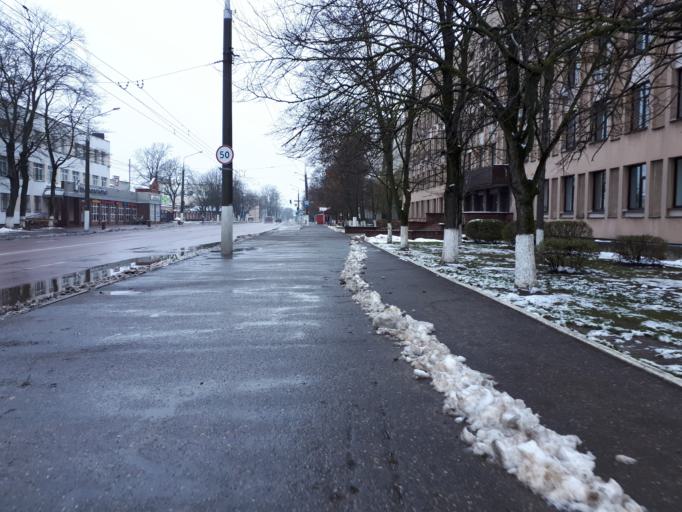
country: BY
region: Vitebsk
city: Vitebsk
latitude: 55.1871
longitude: 30.2187
